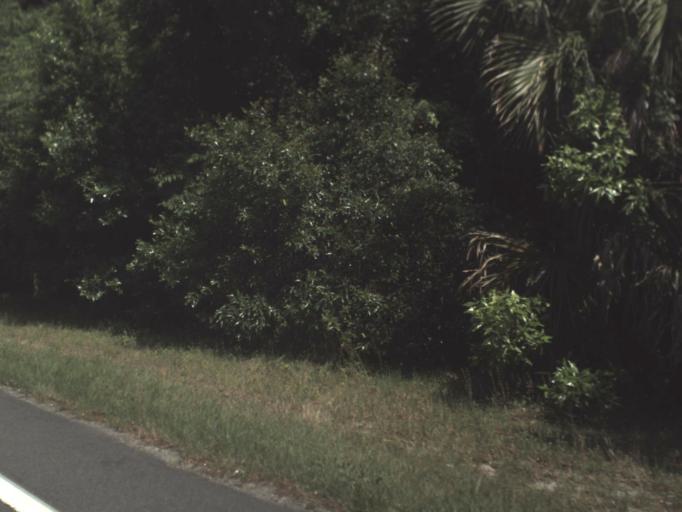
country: US
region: Florida
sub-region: Duval County
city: Atlantic Beach
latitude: 30.3978
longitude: -81.4990
